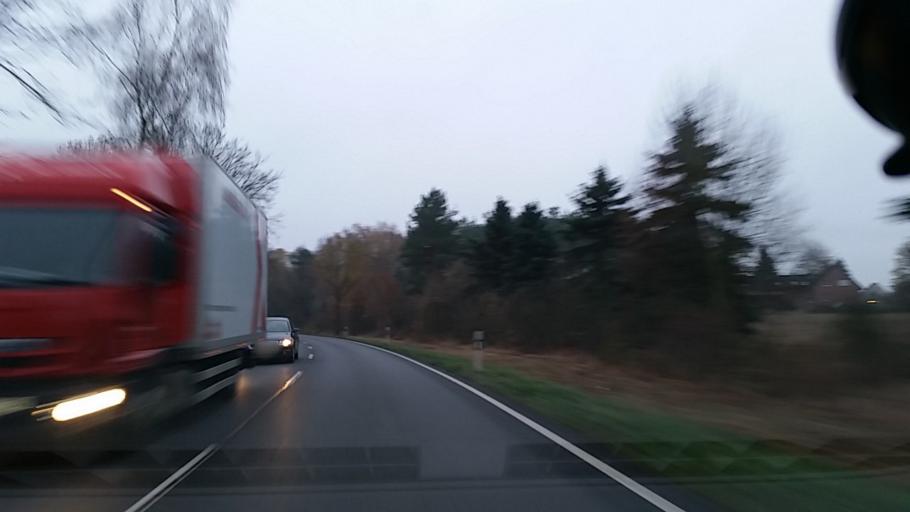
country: DE
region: Lower Saxony
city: Barwedel
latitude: 52.5267
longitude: 10.7779
